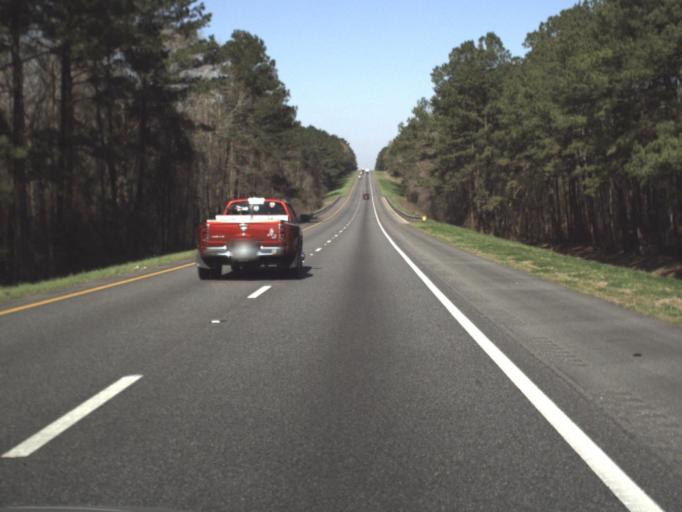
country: US
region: Florida
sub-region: Gadsden County
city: Midway
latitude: 30.5173
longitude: -84.4807
